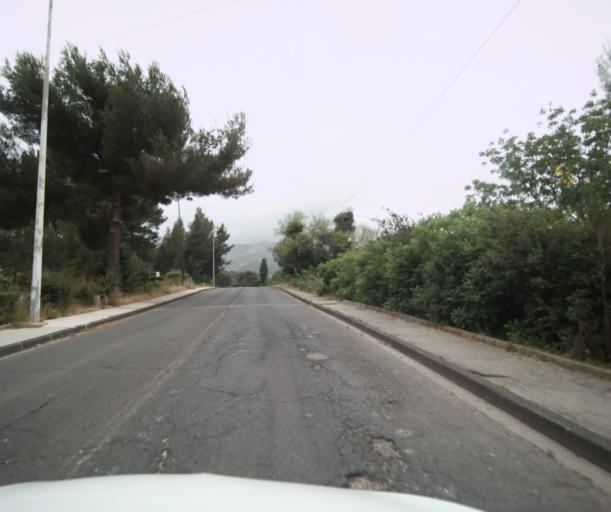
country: FR
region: Provence-Alpes-Cote d'Azur
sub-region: Departement du Var
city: Ollioules
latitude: 43.1358
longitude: 5.8830
